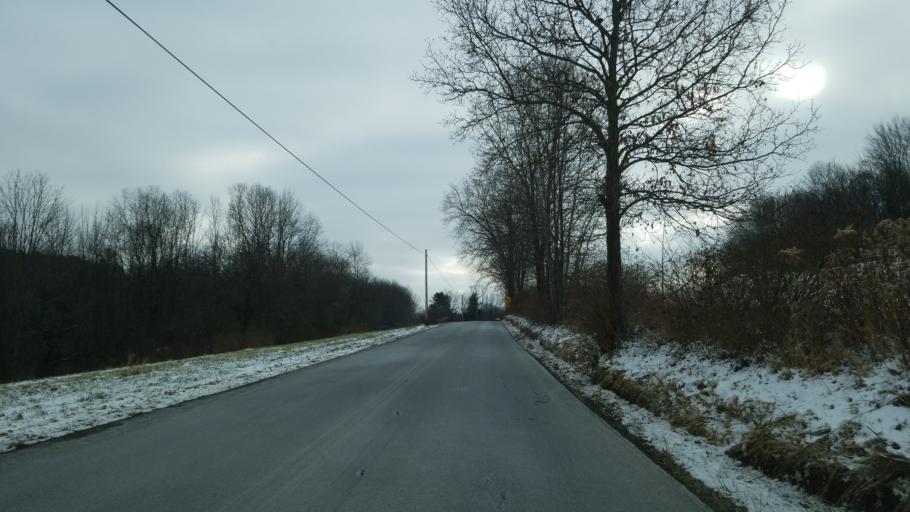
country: US
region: Pennsylvania
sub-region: Clearfield County
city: Sandy
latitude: 41.0988
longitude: -78.7599
